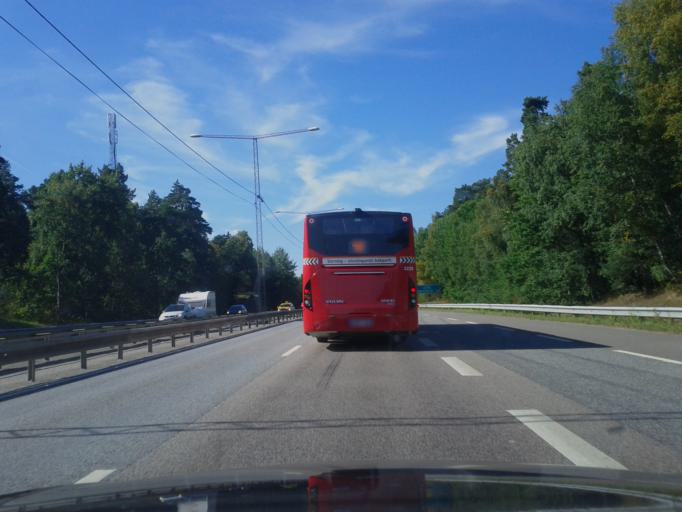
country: SE
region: Stockholm
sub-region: Taby Kommun
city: Taby
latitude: 59.4414
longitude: 18.0909
